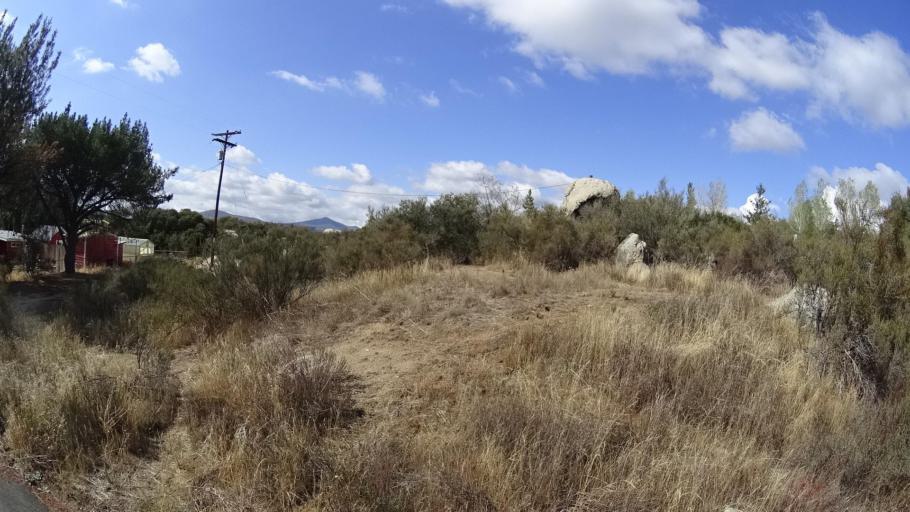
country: US
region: California
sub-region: San Diego County
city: Campo
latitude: 32.6819
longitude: -116.5020
